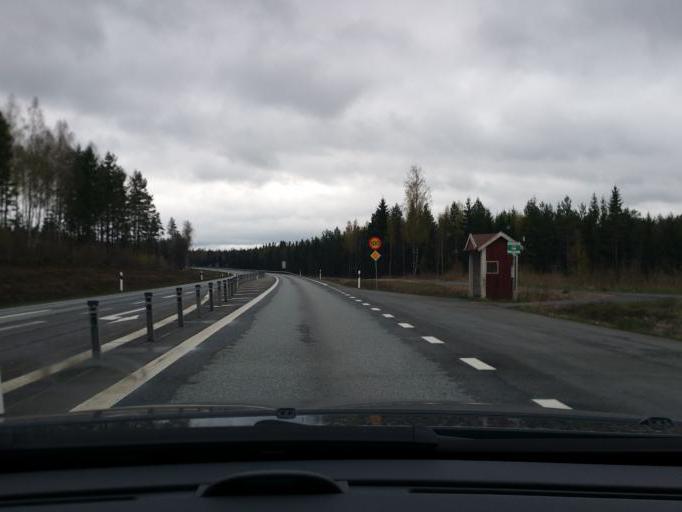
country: SE
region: Kronoberg
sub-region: Vaxjo Kommun
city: Gemla
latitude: 56.9214
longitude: 14.7170
